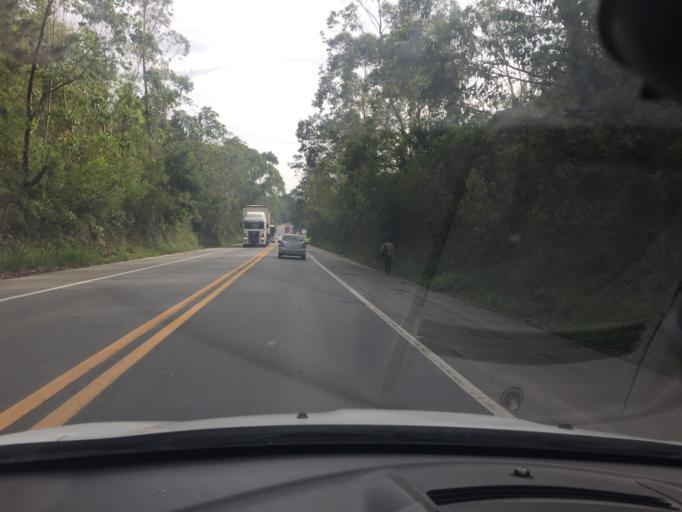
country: BR
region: Sao Paulo
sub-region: Campo Limpo Paulista
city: Campo Limpo Paulista
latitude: -23.1773
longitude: -46.7757
